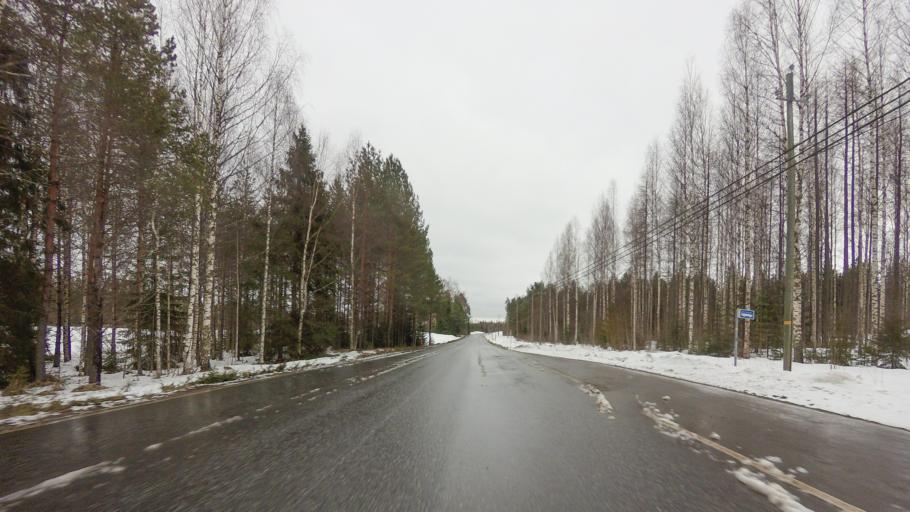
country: FI
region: Southern Savonia
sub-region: Savonlinna
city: Savonlinna
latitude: 61.9467
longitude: 28.8662
